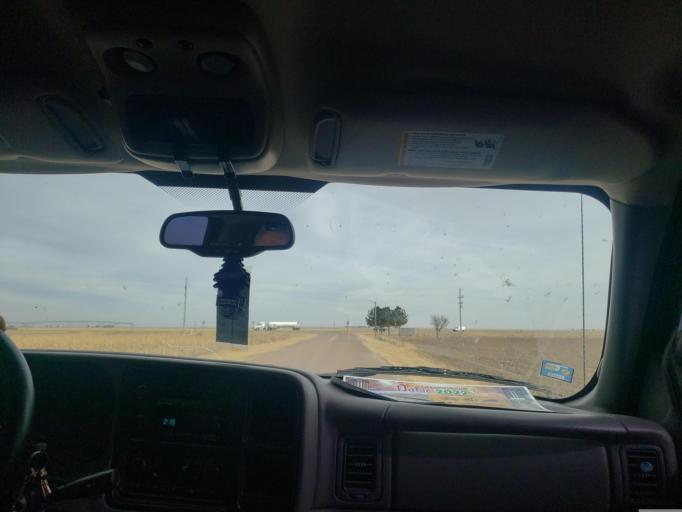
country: US
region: Kansas
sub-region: Finney County
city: Garden City
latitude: 37.9241
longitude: -100.7110
